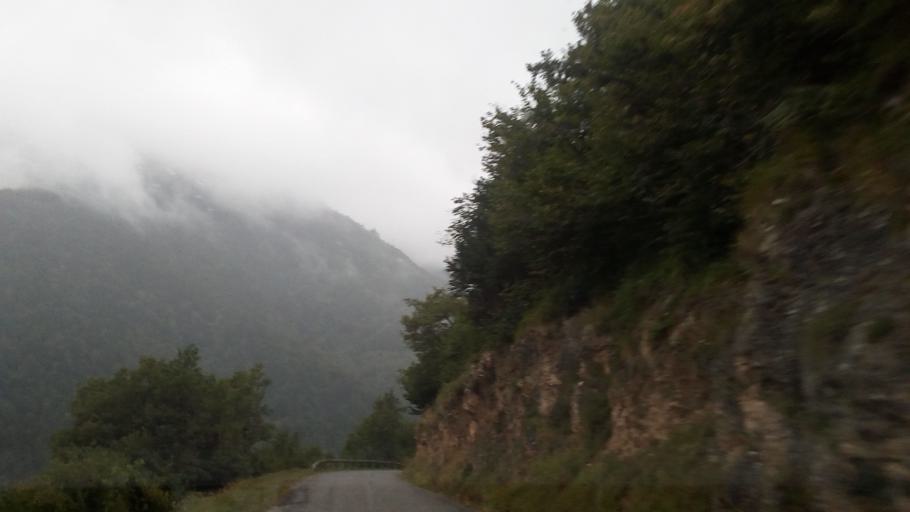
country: FR
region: Midi-Pyrenees
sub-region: Departement des Hautes-Pyrenees
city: Saint-Lary-Soulan
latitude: 42.8793
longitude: 0.3346
